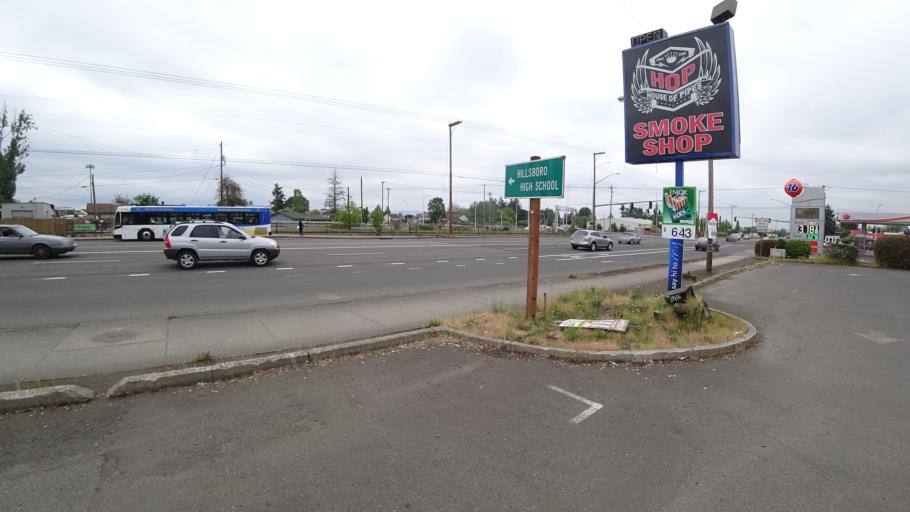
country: US
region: Oregon
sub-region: Washington County
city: Aloha
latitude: 45.5006
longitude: -122.9296
